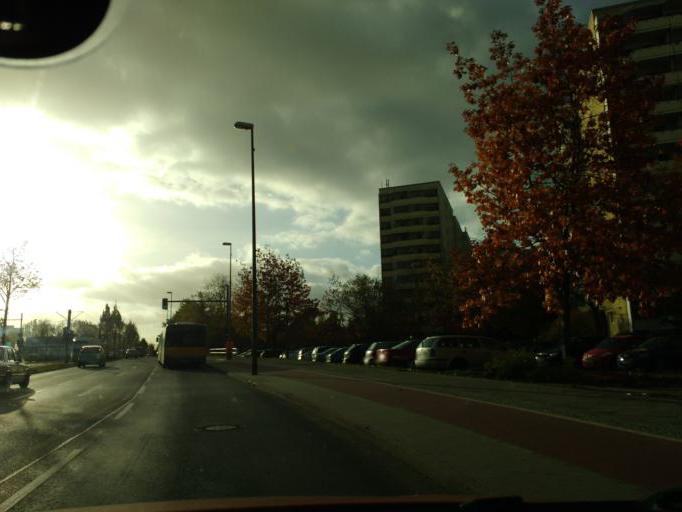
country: DE
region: Berlin
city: Marzahn
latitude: 52.5474
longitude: 13.5761
